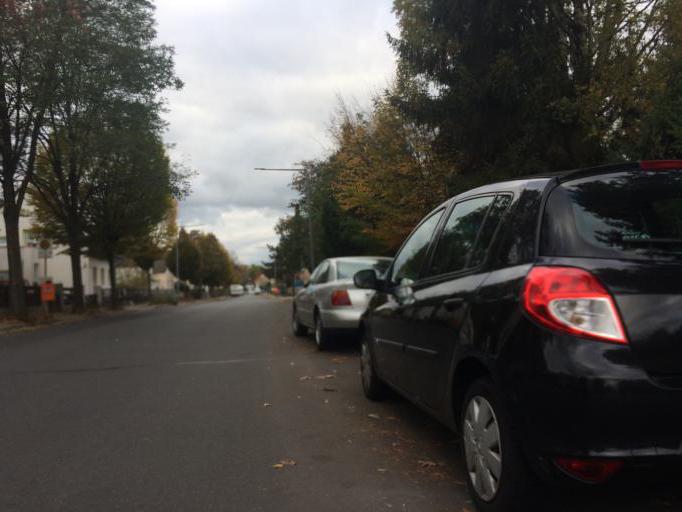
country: DE
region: Berlin
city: Markisches Viertel
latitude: 52.5931
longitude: 13.3431
